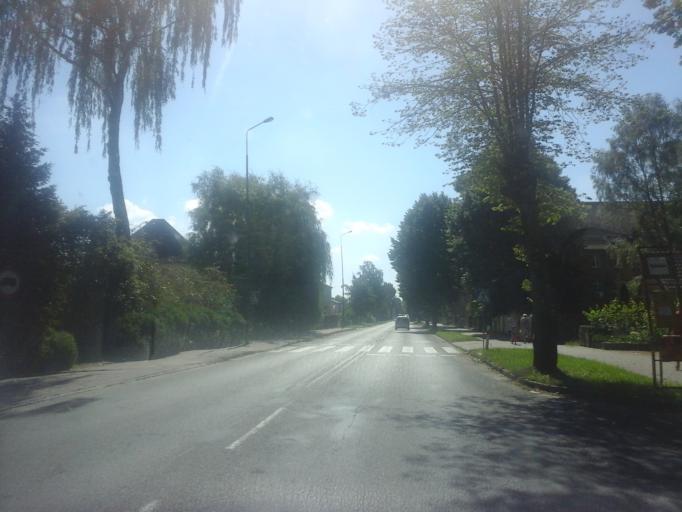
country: PL
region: West Pomeranian Voivodeship
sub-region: Powiat bialogardzki
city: Bialogard
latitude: 54.0114
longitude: 15.9646
